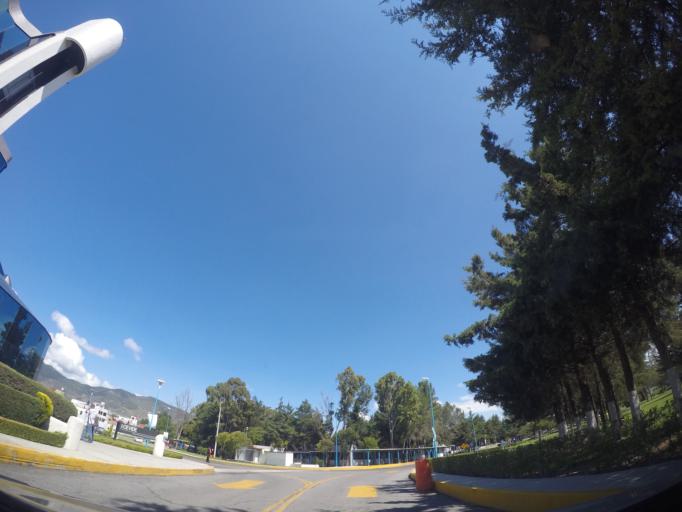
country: MX
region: Hidalgo
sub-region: Mineral de la Reforma
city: Campestre Villas del Alamo
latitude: 20.0964
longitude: -98.7143
